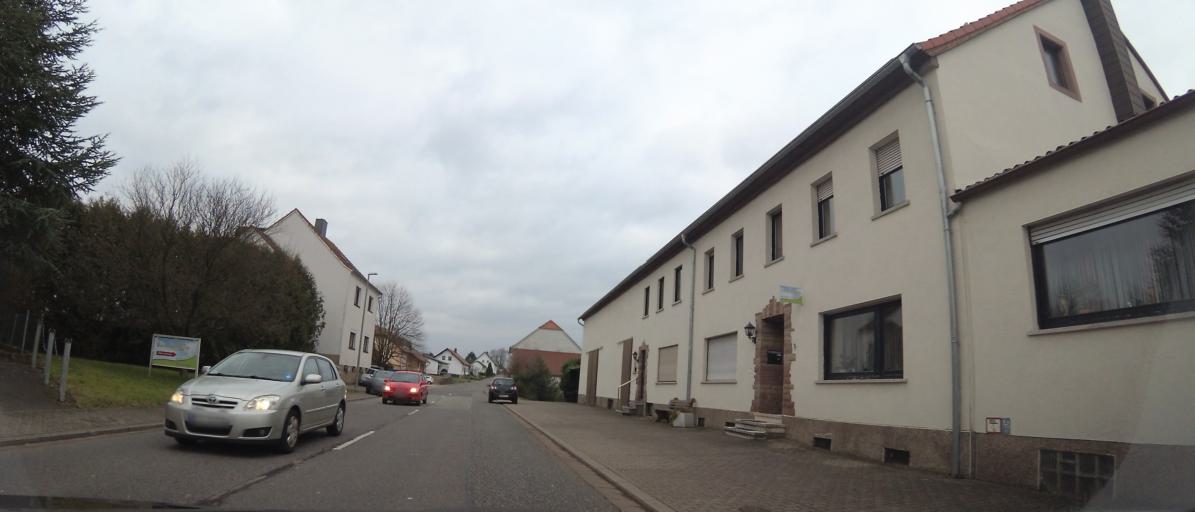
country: DE
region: Saarland
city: Heusweiler
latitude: 49.3474
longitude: 6.9614
